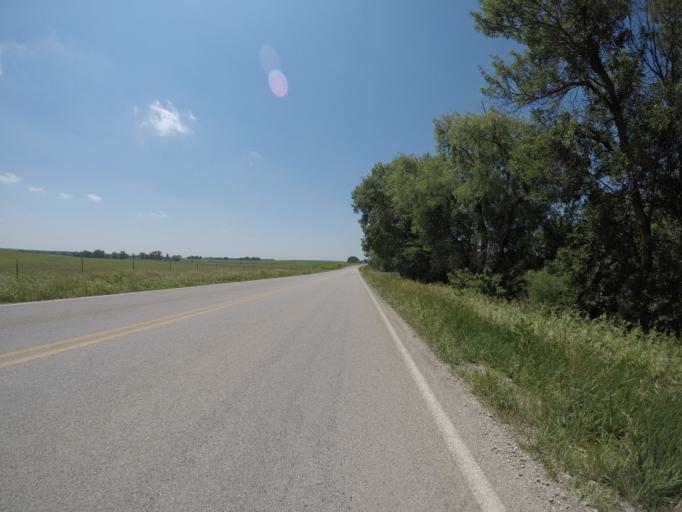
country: US
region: Kansas
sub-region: Pottawatomie County
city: Westmoreland
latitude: 39.3107
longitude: -96.4363
